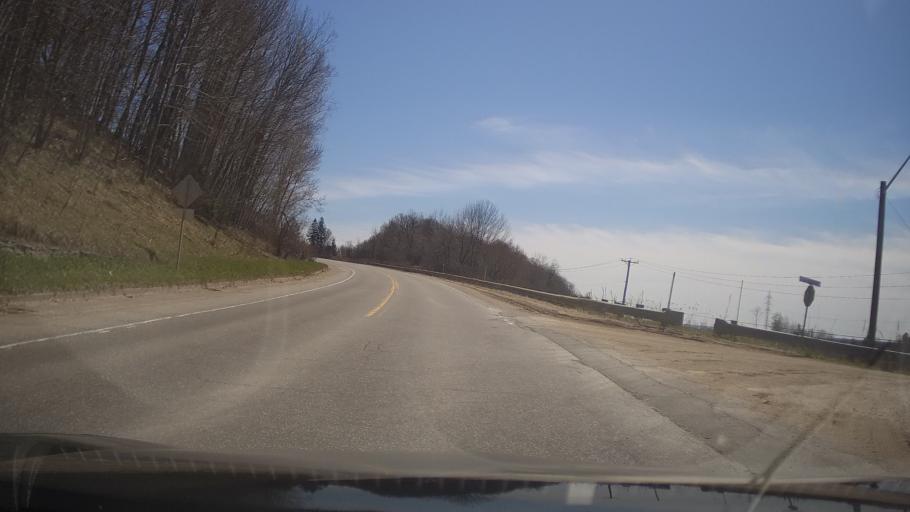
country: CA
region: Quebec
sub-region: Outaouais
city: Wakefield
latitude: 45.5482
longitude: -76.0842
